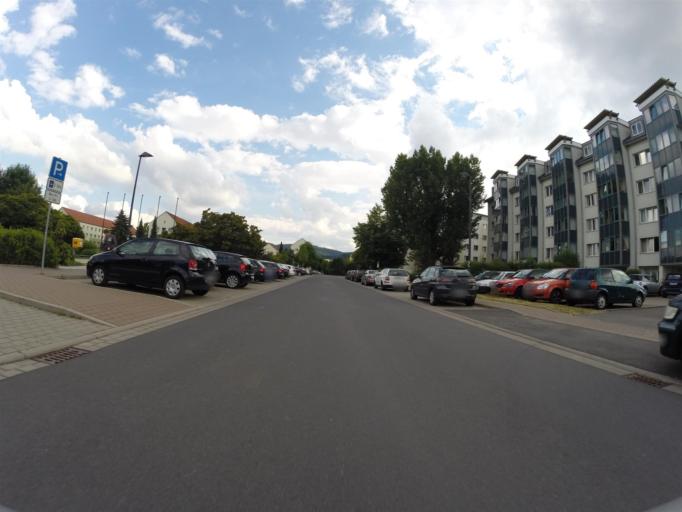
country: DE
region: Thuringia
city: Neuhaus
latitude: 50.6830
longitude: 10.9330
